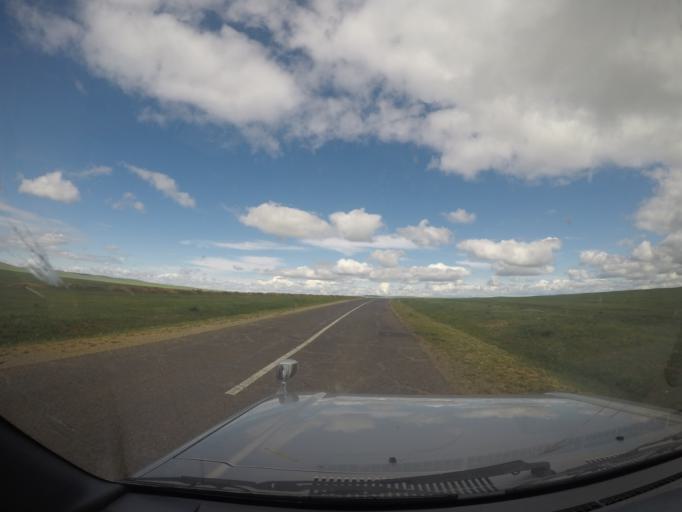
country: MN
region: Hentiy
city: Avraga
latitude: 47.4669
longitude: 109.5831
